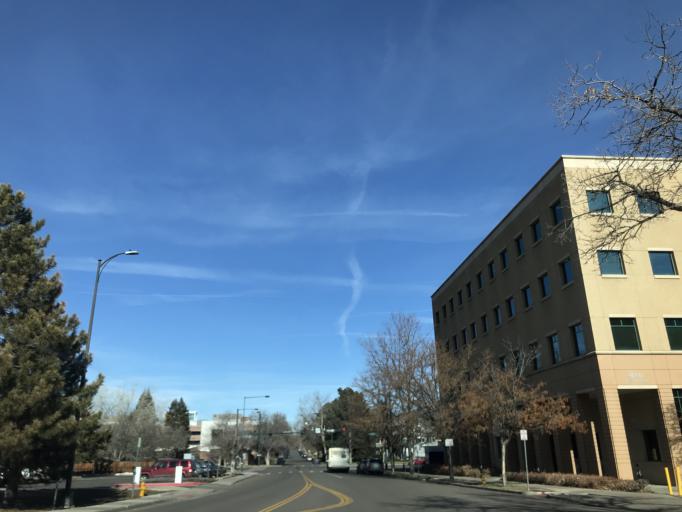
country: US
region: Colorado
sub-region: Arapahoe County
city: Glendale
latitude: 39.7326
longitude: -104.9350
